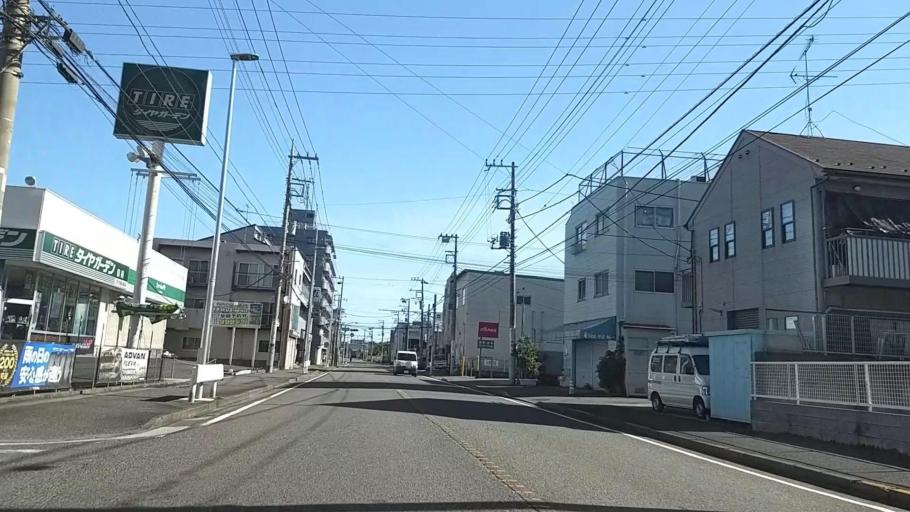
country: JP
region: Kanagawa
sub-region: Kawasaki-shi
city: Kawasaki
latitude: 35.5347
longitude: 139.6528
